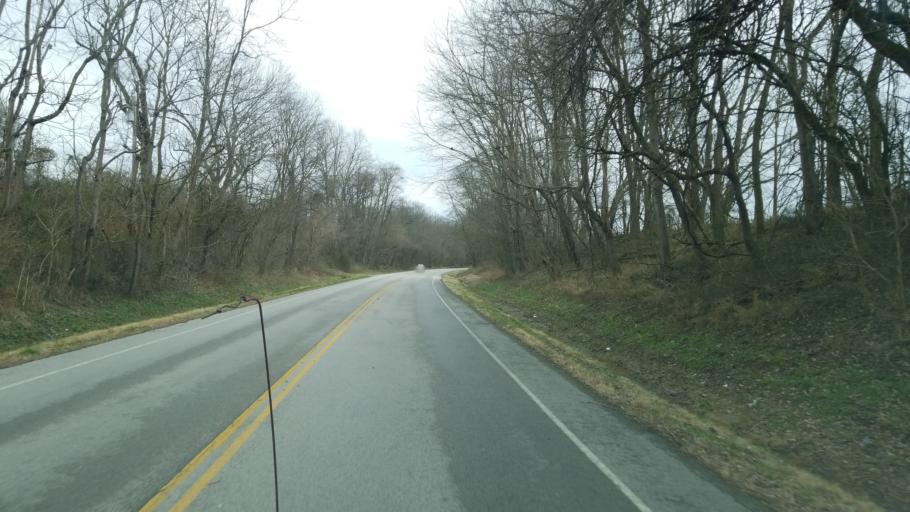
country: US
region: Kentucky
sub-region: Bracken County
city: Augusta
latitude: 38.7891
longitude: -83.9427
